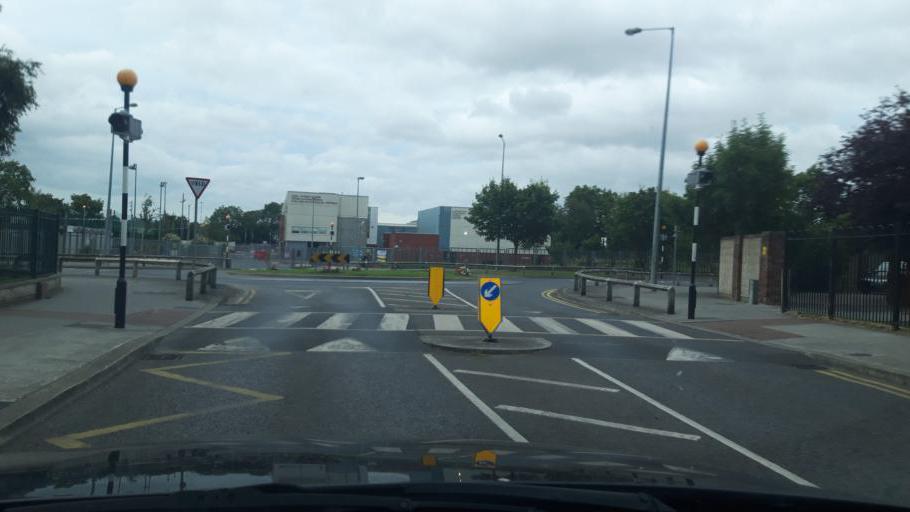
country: IE
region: Leinster
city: Hartstown
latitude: 53.4033
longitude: -6.4256
